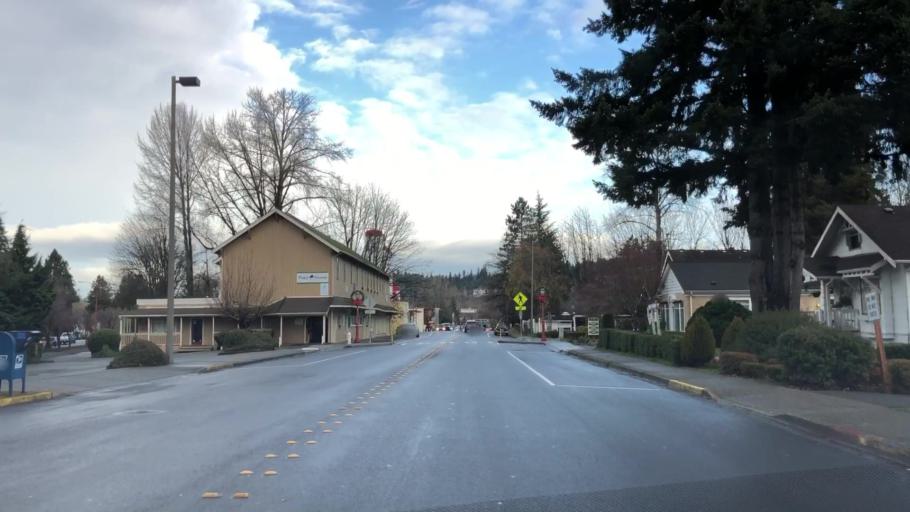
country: US
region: Washington
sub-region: King County
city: Issaquah
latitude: 47.5342
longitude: -122.0364
